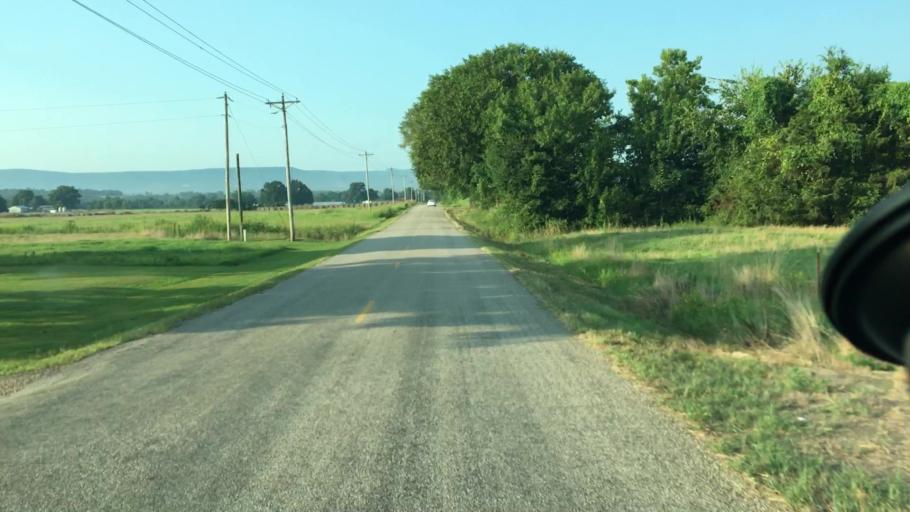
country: US
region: Arkansas
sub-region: Johnson County
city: Coal Hill
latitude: 35.3438
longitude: -93.6136
